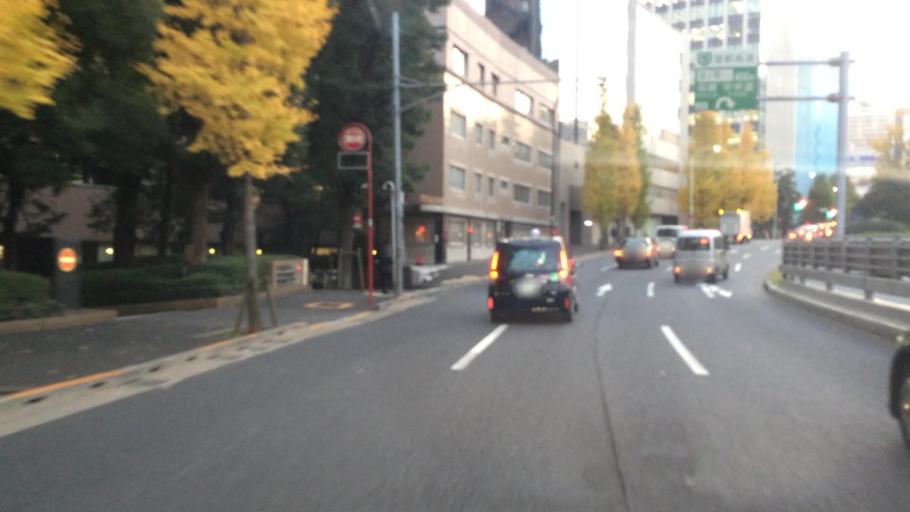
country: JP
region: Tokyo
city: Tokyo
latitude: 35.6724
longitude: 139.7465
